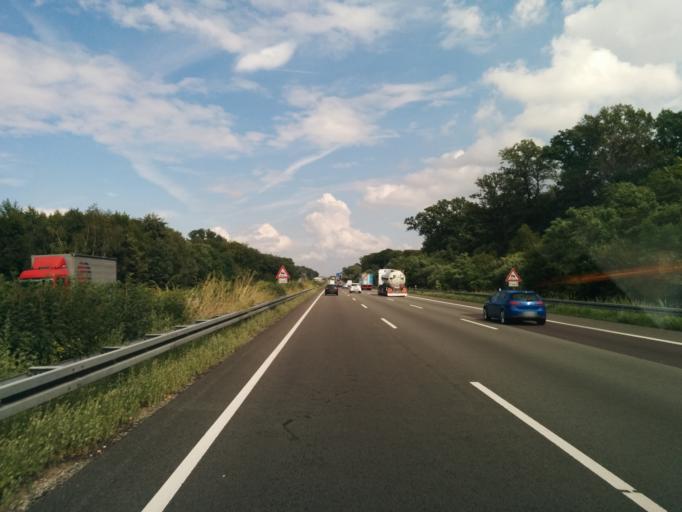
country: DE
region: Lower Saxony
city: Lehre
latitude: 52.3089
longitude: 10.6762
